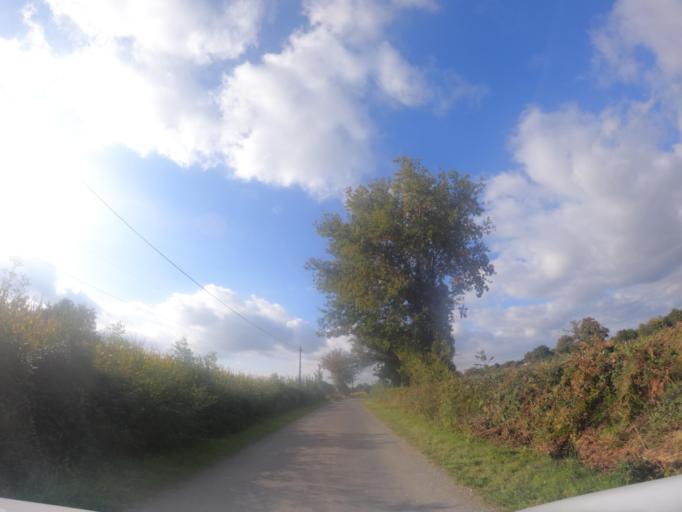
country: FR
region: Poitou-Charentes
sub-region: Departement des Deux-Sevres
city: La Foret-sur-Sevre
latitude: 46.7798
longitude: -0.6140
